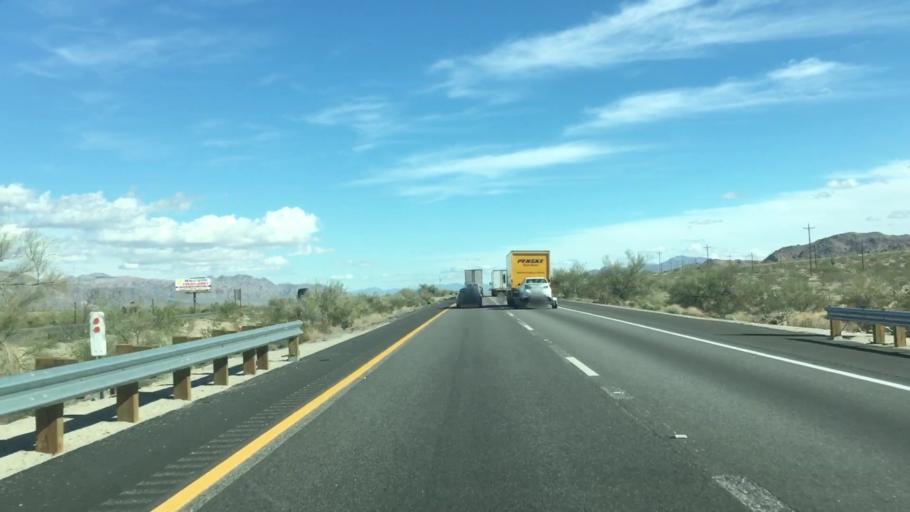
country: US
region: California
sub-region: Riverside County
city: Mecca
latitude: 33.6615
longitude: -115.7113
